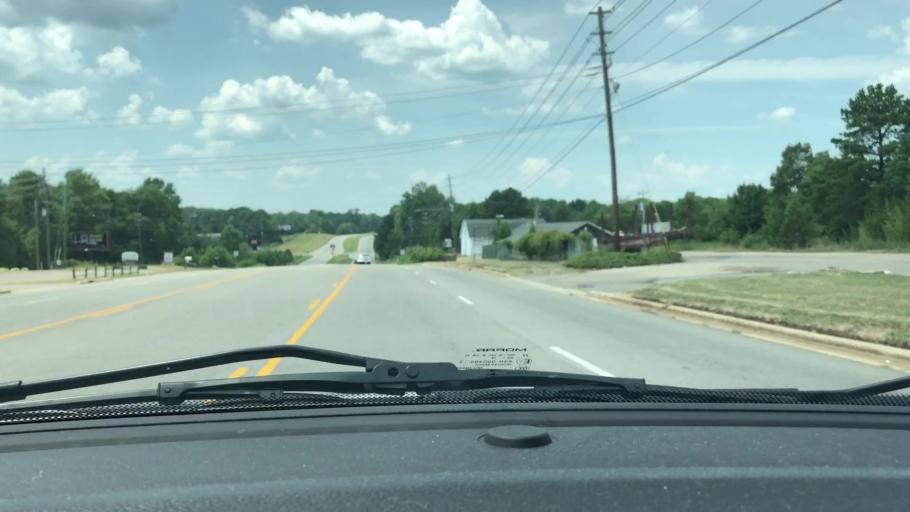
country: US
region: North Carolina
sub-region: Lee County
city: Sanford
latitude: 35.4977
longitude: -79.1988
